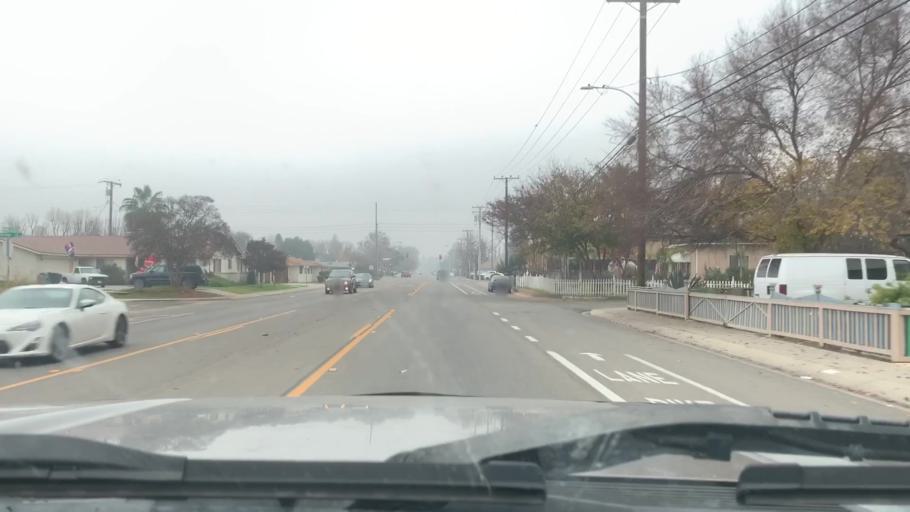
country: US
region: California
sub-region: Tulare County
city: Visalia
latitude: 36.3150
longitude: -119.3054
